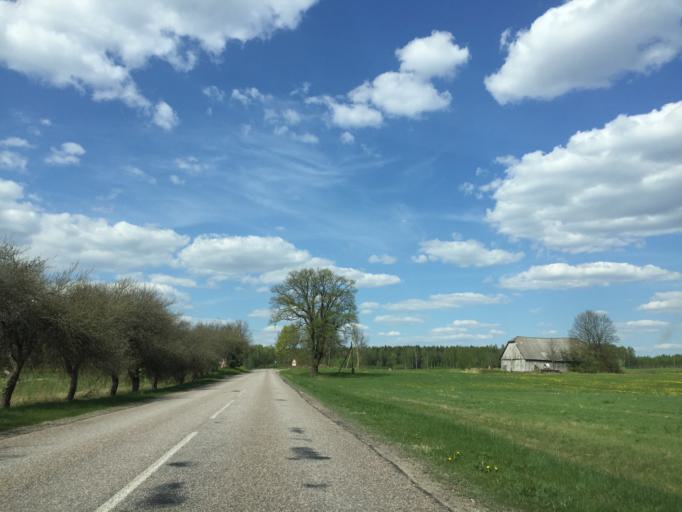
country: LV
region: Limbazu Rajons
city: Limbazi
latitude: 57.3984
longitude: 24.6908
